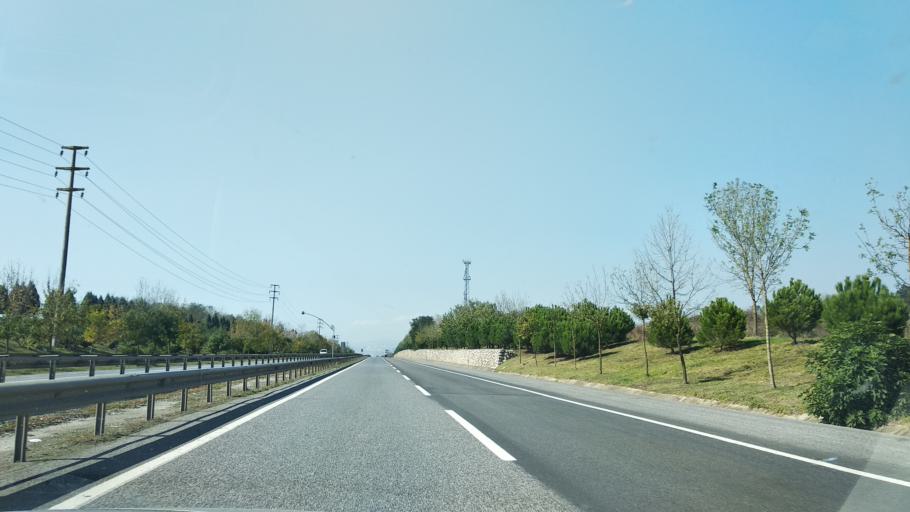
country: TR
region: Kocaeli
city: Derbent
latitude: 40.7438
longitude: 30.0800
